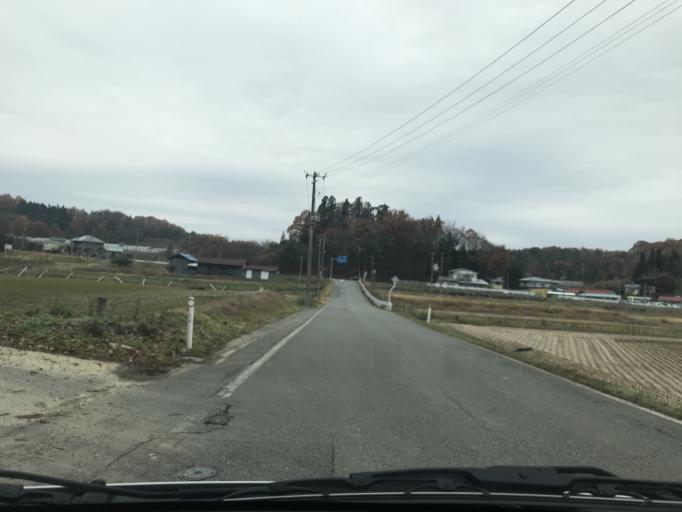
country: JP
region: Iwate
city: Kitakami
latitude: 39.2919
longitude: 141.1745
